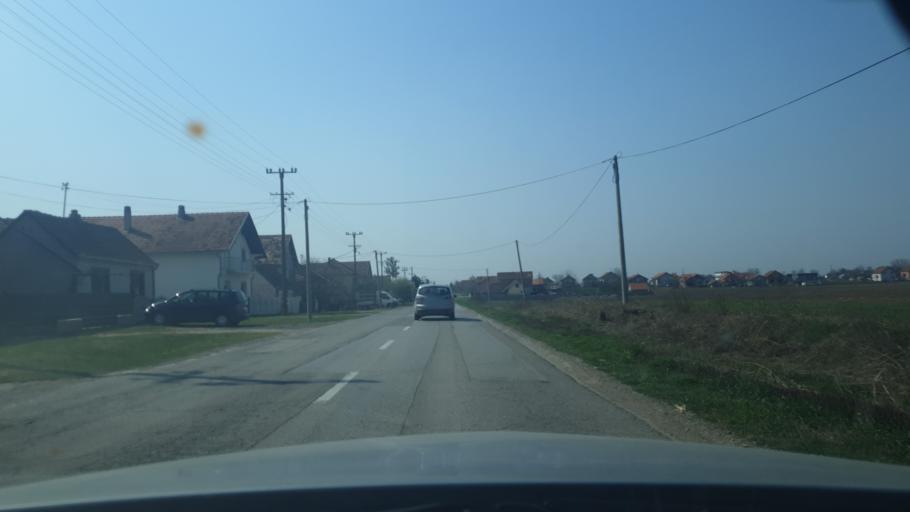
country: RS
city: Ljukovo
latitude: 45.0234
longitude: 20.0397
